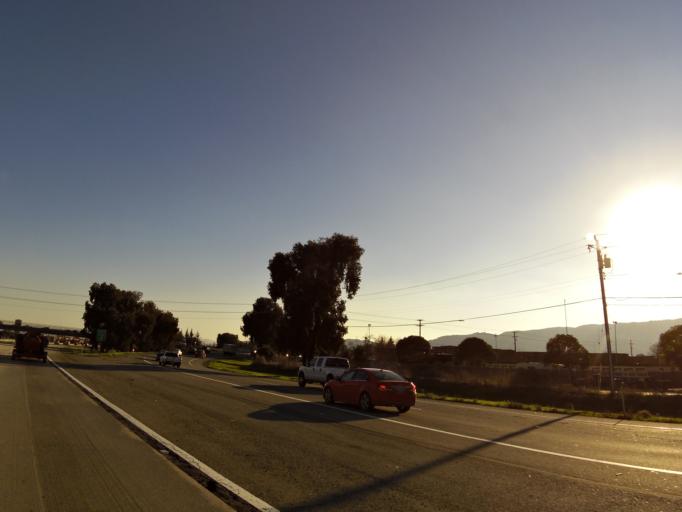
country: US
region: California
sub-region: Santa Clara County
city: Gilroy
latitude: 37.0058
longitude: -121.5579
